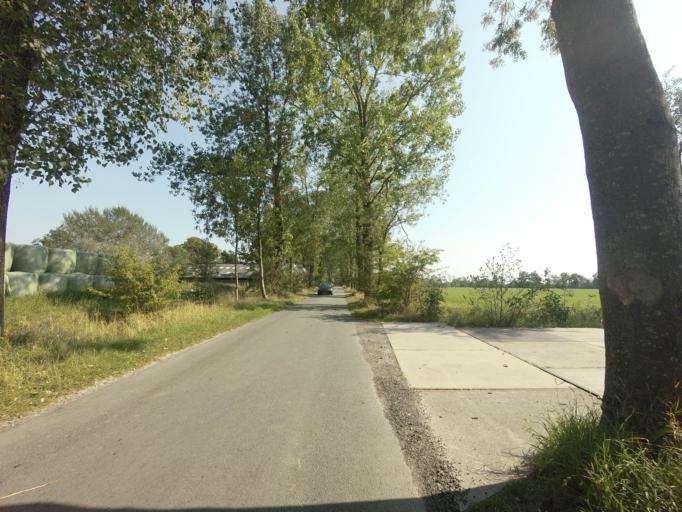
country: NL
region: Groningen
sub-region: Gemeente Zuidhorn
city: Zuidhorn
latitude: 53.2381
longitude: 6.4132
